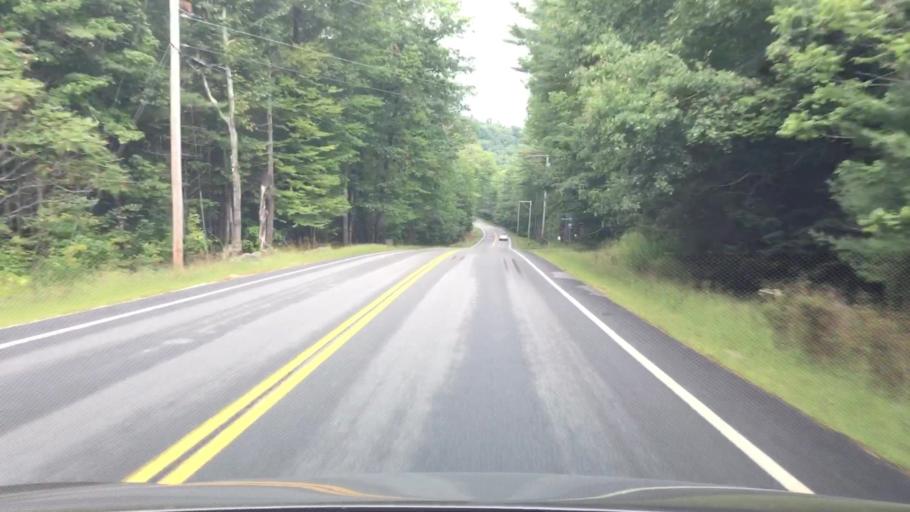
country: US
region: Maine
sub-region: Oxford County
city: Hartford
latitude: 44.3398
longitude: -70.2944
